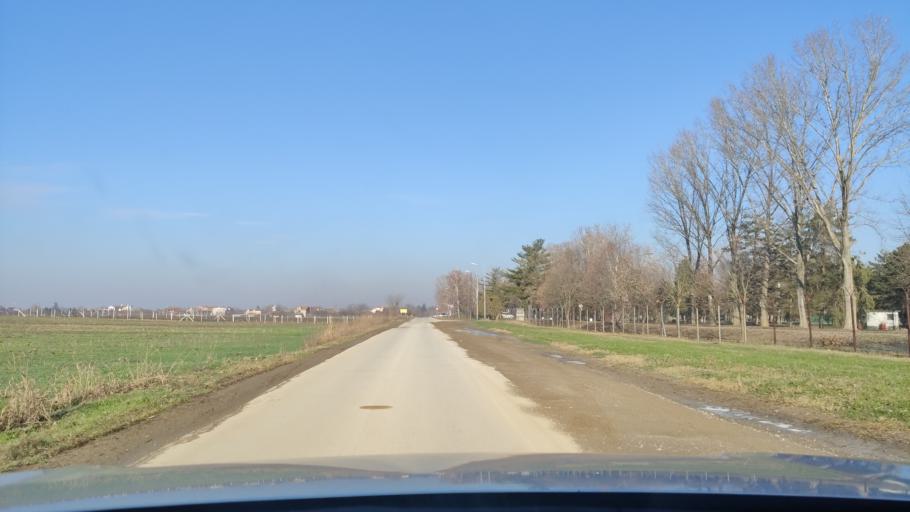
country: RS
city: Ostruznica
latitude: 44.7411
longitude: 20.2742
